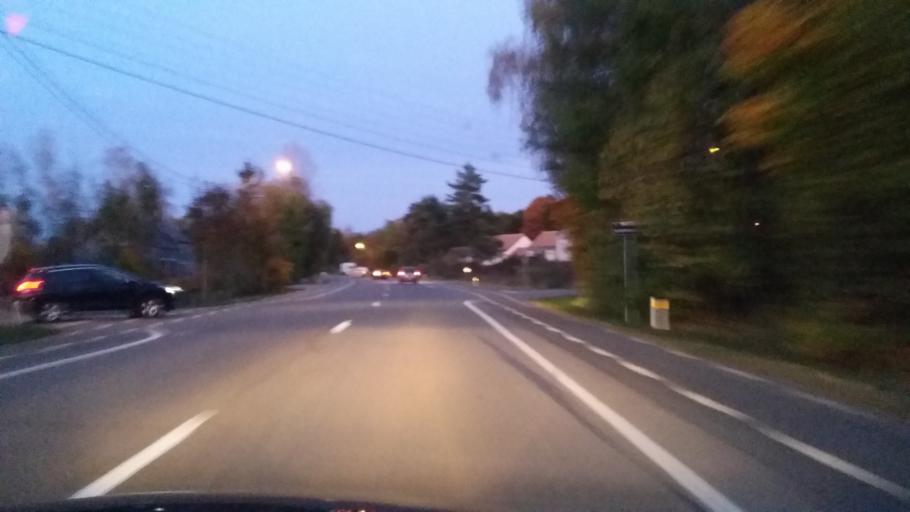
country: BE
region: Wallonia
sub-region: Province du Luxembourg
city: Saint-Leger
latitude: 49.6779
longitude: 5.7035
